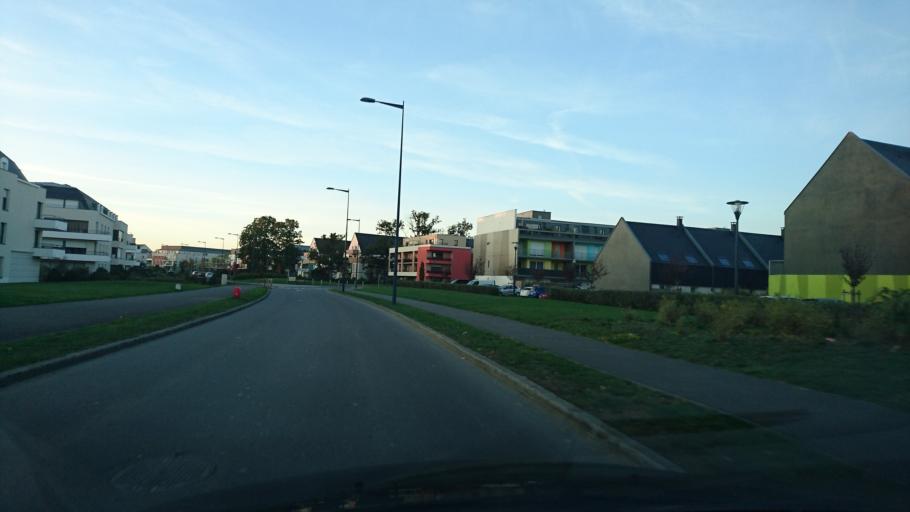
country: FR
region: Brittany
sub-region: Departement d'Ille-et-Vilaine
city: Bruz
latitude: 48.0258
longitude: -1.7548
